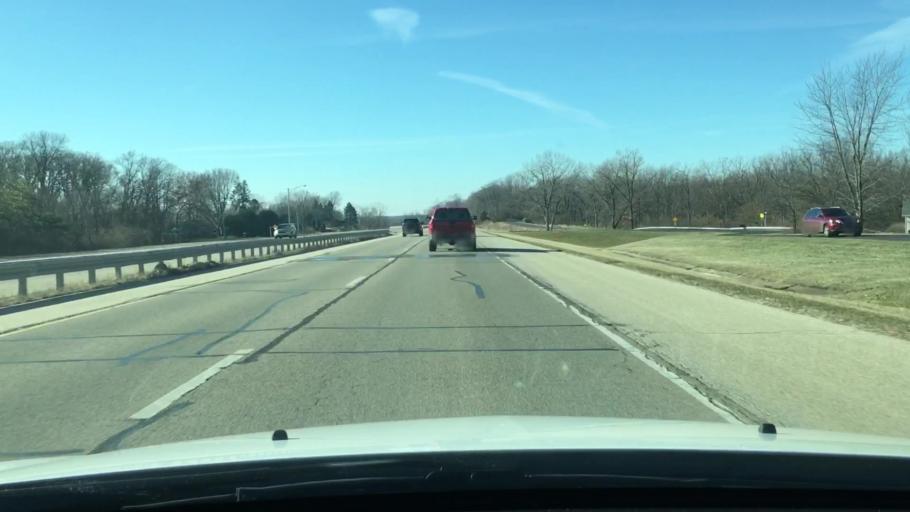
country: US
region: Illinois
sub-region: Woodford County
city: Germantown Hills
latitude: 40.7561
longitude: -89.4964
